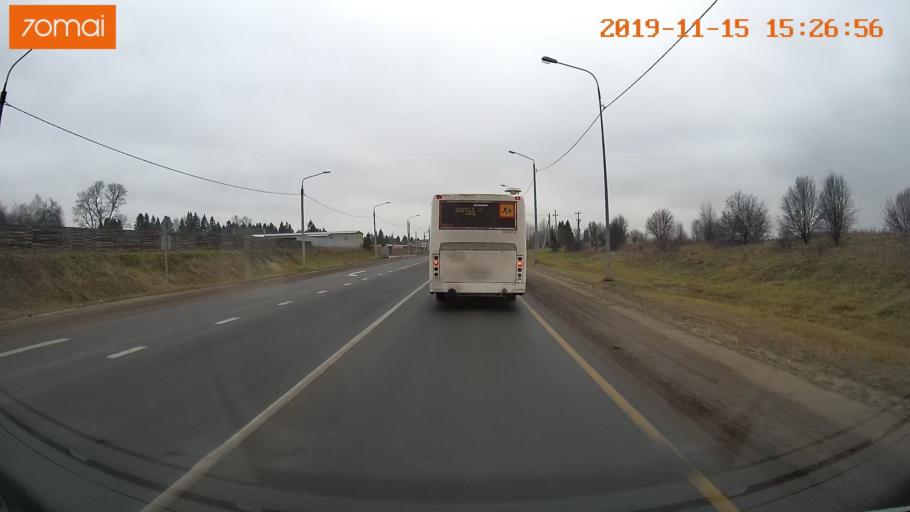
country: RU
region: Jaroslavl
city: Danilov
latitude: 58.1470
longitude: 40.1477
